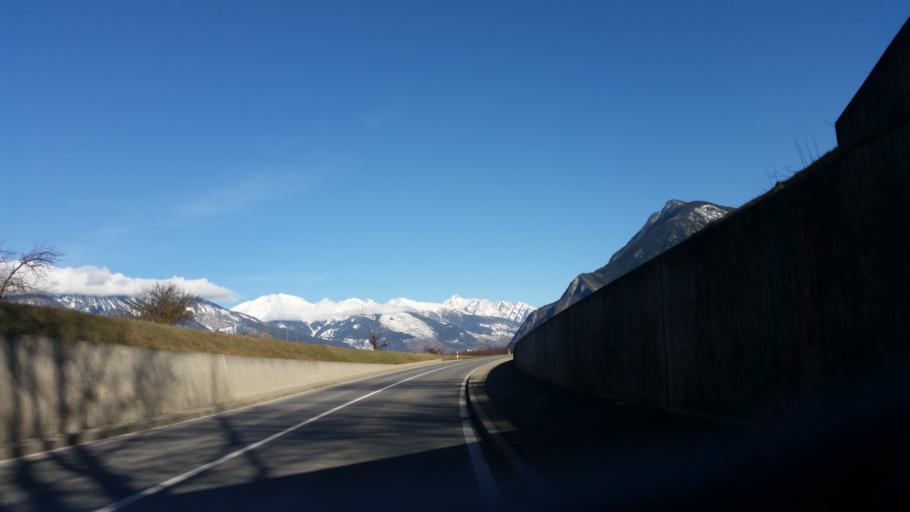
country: CH
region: Valais
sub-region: Sierre District
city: Chalais
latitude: 46.2654
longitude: 7.4911
